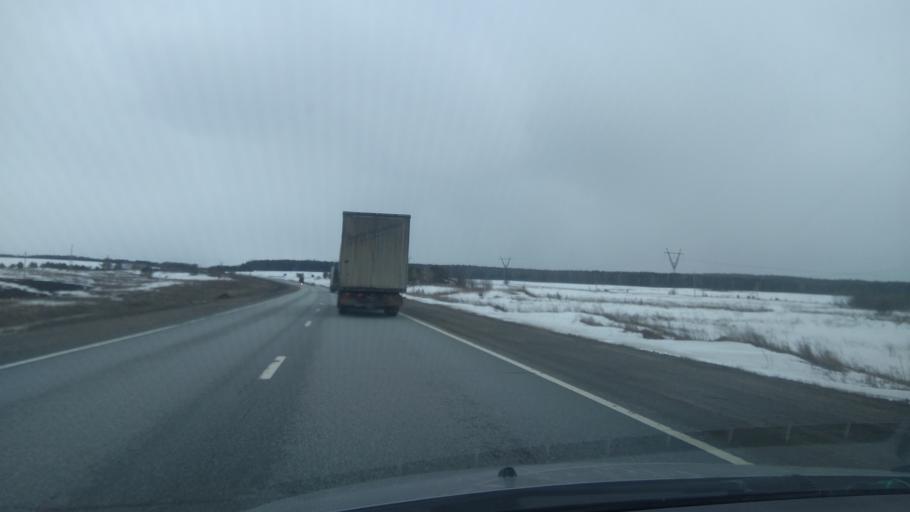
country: RU
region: Sverdlovsk
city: Achit
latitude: 56.8881
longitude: 57.6124
